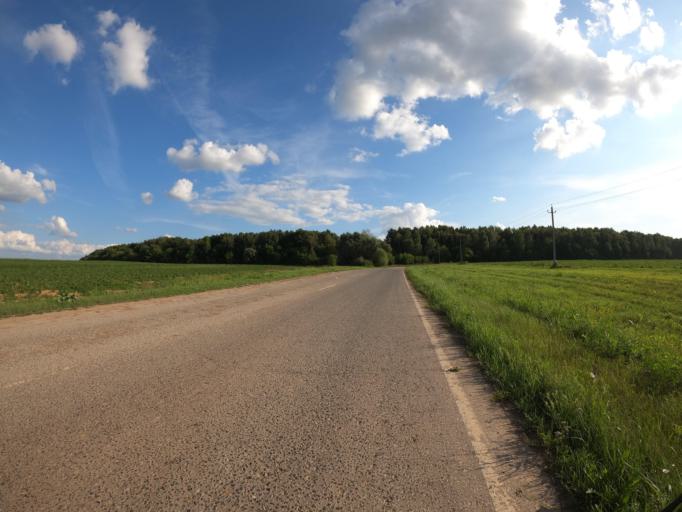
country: RU
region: Moskovskaya
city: Meshcherino
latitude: 55.1832
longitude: 38.4713
